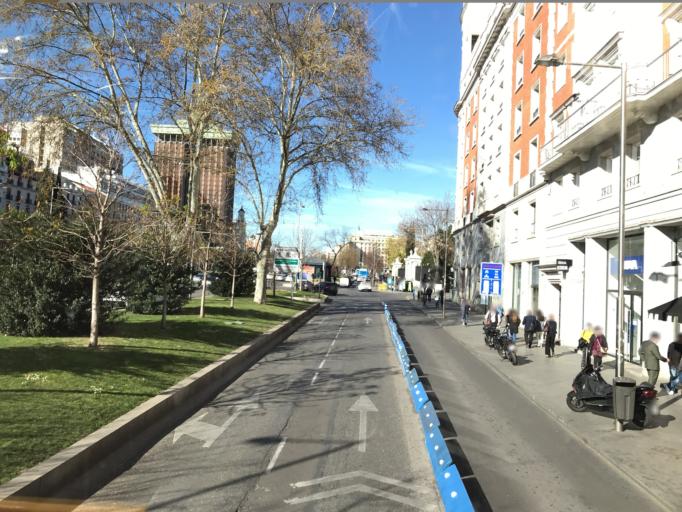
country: ES
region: Madrid
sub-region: Provincia de Madrid
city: City Center
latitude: 40.4224
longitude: -3.6912
